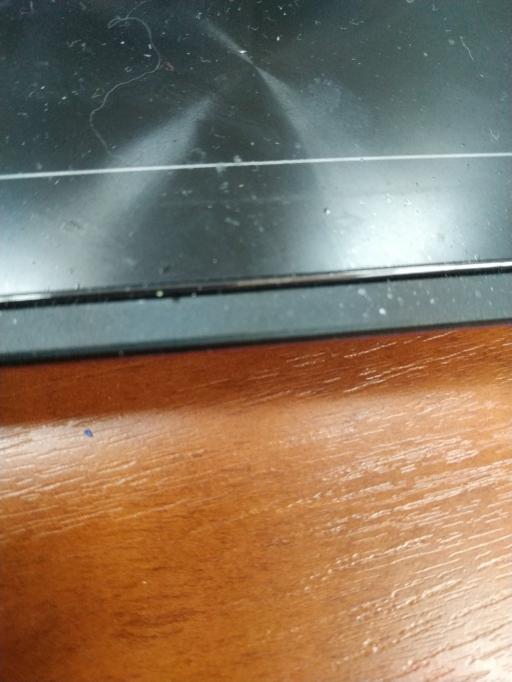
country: RU
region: Tula
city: Zaokskiy
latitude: 54.7265
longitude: 37.5052
